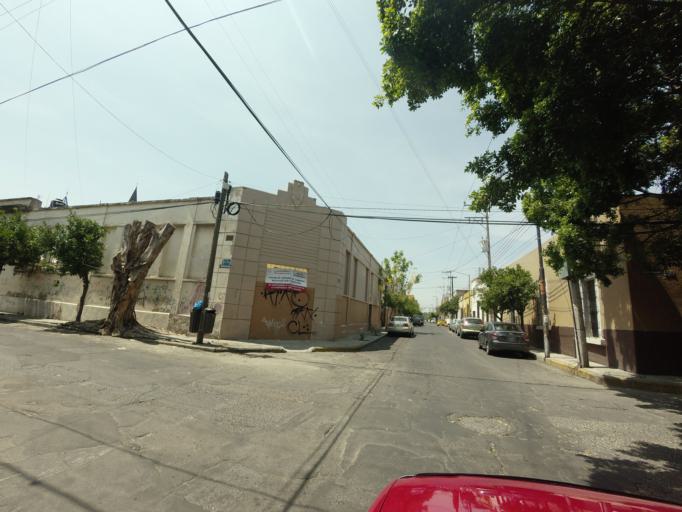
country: MX
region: Jalisco
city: Guadalajara
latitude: 20.6867
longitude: -103.3410
